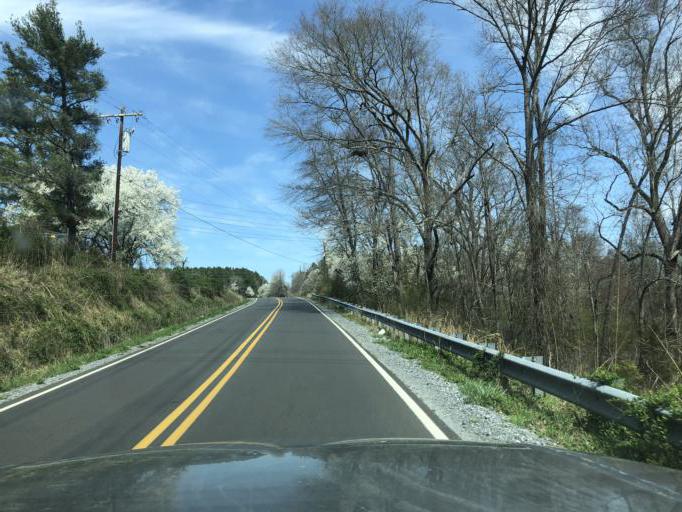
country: US
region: North Carolina
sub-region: Cleveland County
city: Shelby
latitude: 35.2567
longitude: -81.5429
